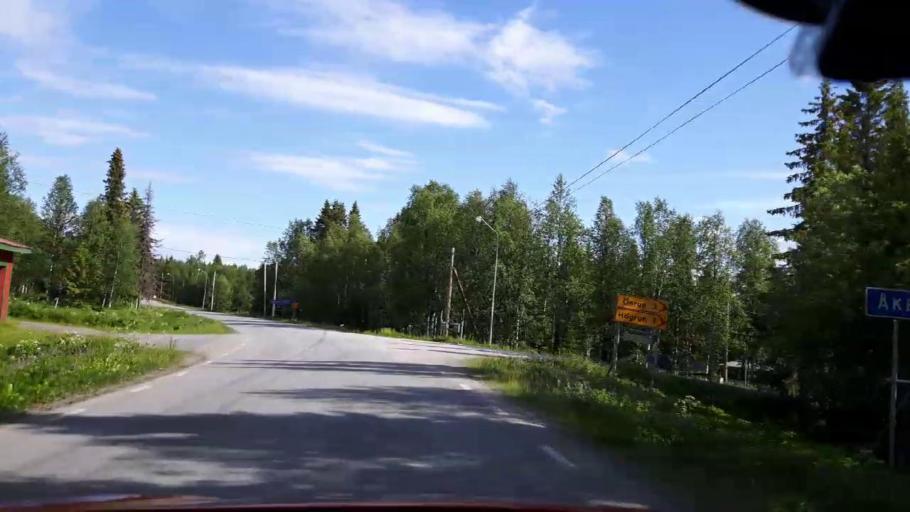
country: SE
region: Jaemtland
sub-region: Krokoms Kommun
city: Valla
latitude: 63.7724
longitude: 14.0477
